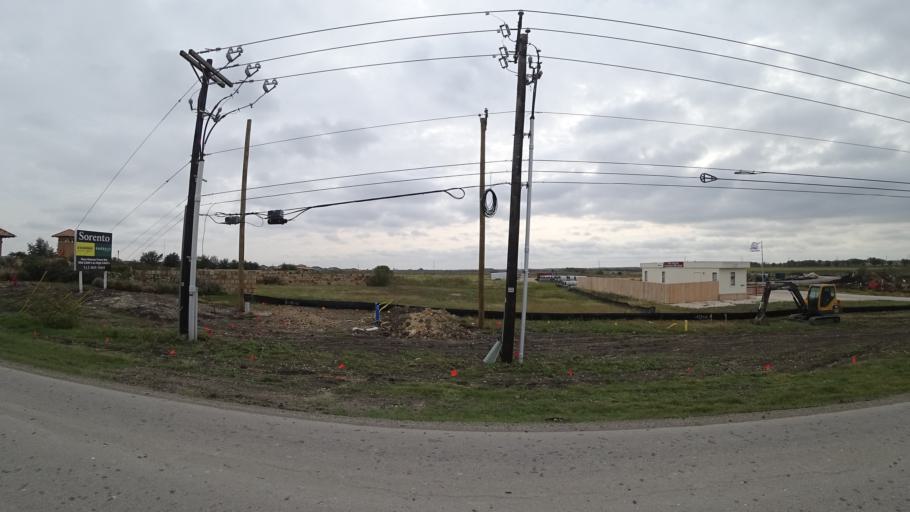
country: US
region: Texas
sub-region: Travis County
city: Pflugerville
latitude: 30.4421
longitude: -97.5648
